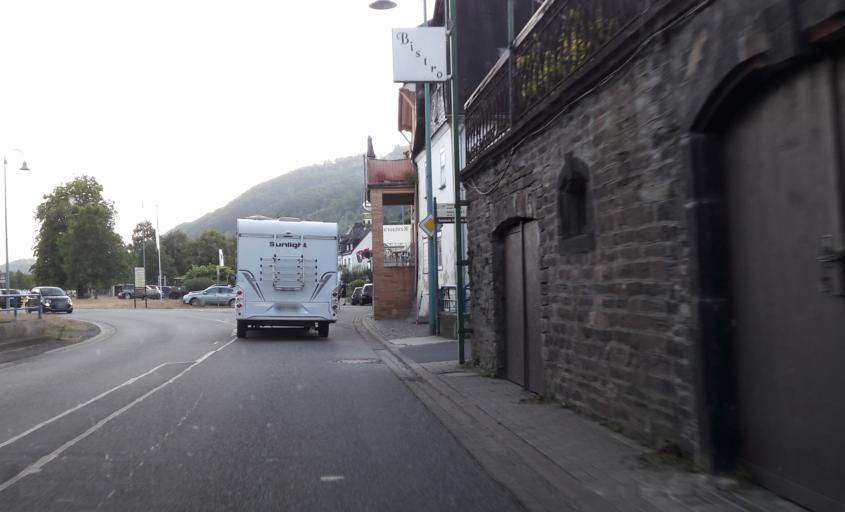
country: DE
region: Rheinland-Pfalz
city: Sankt Aldegund
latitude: 50.0826
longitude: 7.1315
